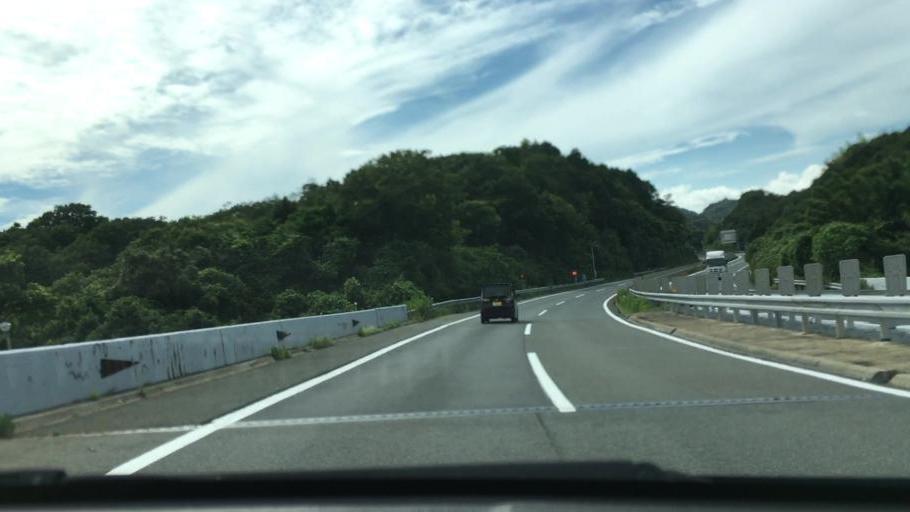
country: JP
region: Yamaguchi
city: Ogori-shimogo
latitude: 34.1267
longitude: 131.3841
